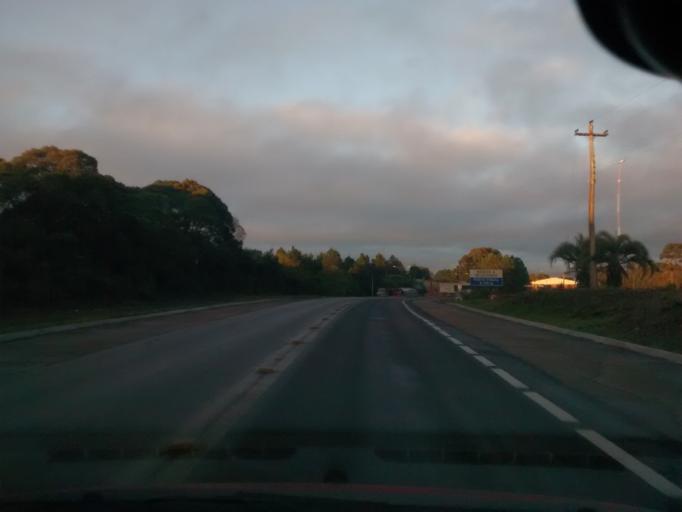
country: BR
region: Rio Grande do Sul
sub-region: Vacaria
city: Estrela
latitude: -28.2636
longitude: -50.7862
